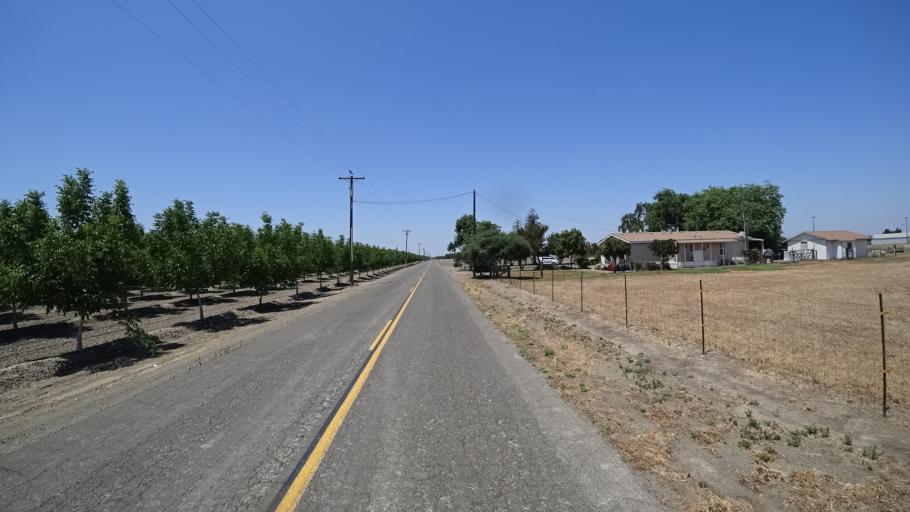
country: US
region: California
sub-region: Fresno County
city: Laton
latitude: 36.3865
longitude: -119.7356
